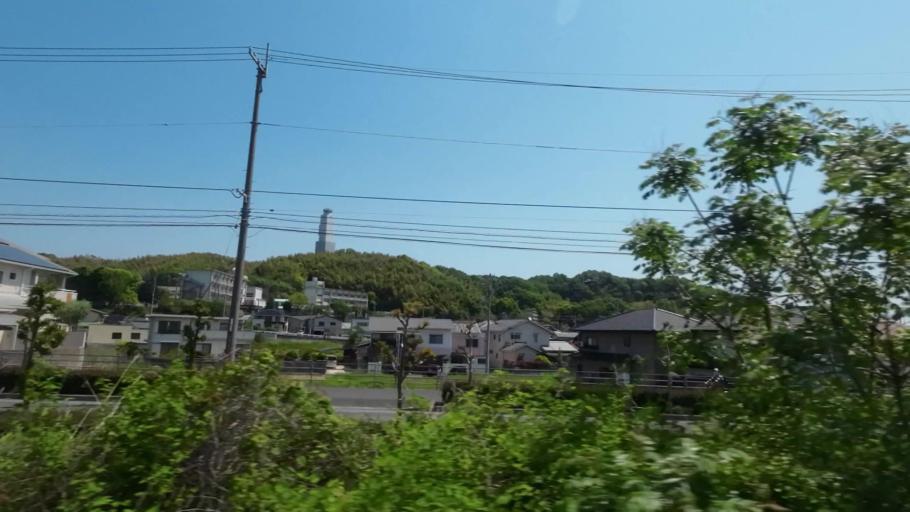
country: JP
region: Ehime
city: Hojo
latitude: 34.0879
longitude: 132.9841
